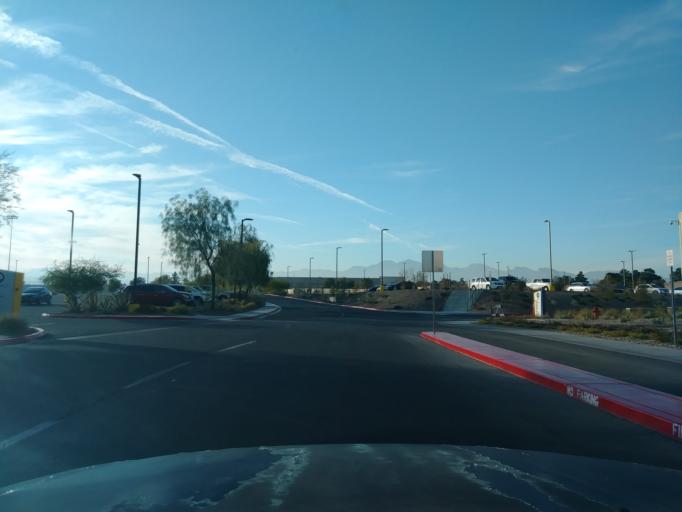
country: US
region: Nevada
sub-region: Clark County
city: Spring Valley
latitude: 36.1540
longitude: -115.2321
